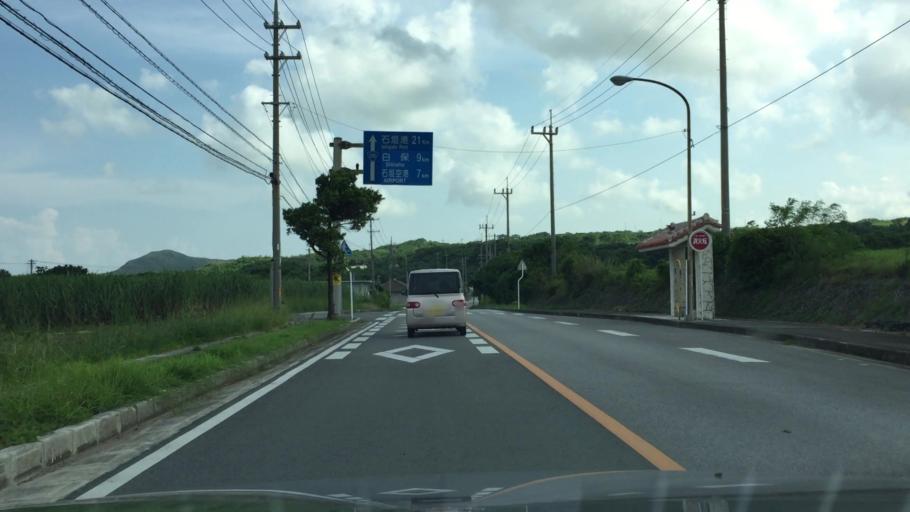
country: JP
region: Okinawa
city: Ishigaki
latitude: 24.4347
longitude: 124.2487
